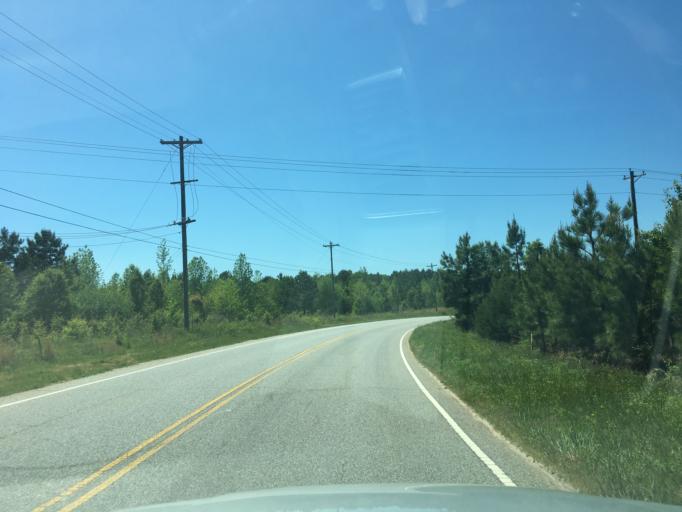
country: US
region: South Carolina
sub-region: Spartanburg County
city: Duncan
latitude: 34.8832
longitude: -82.1853
